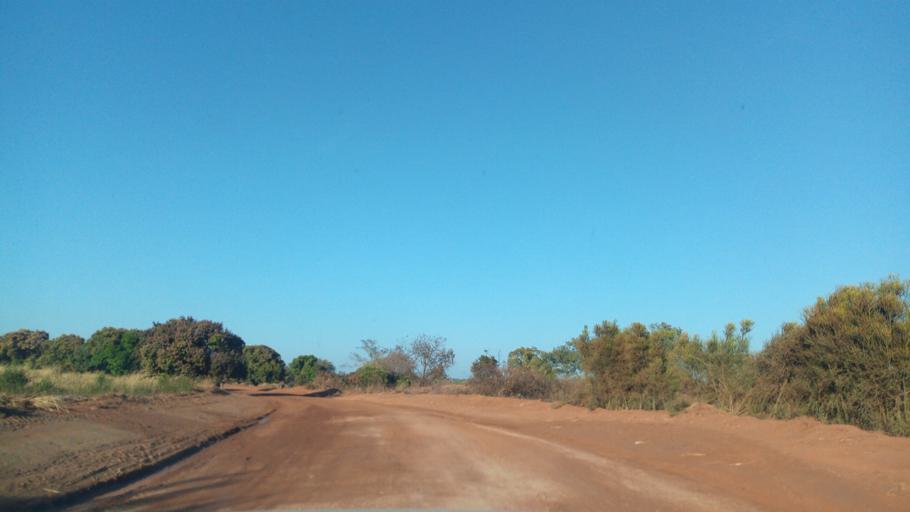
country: ZM
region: Luapula
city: Mwense
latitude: -10.4226
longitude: 28.6021
